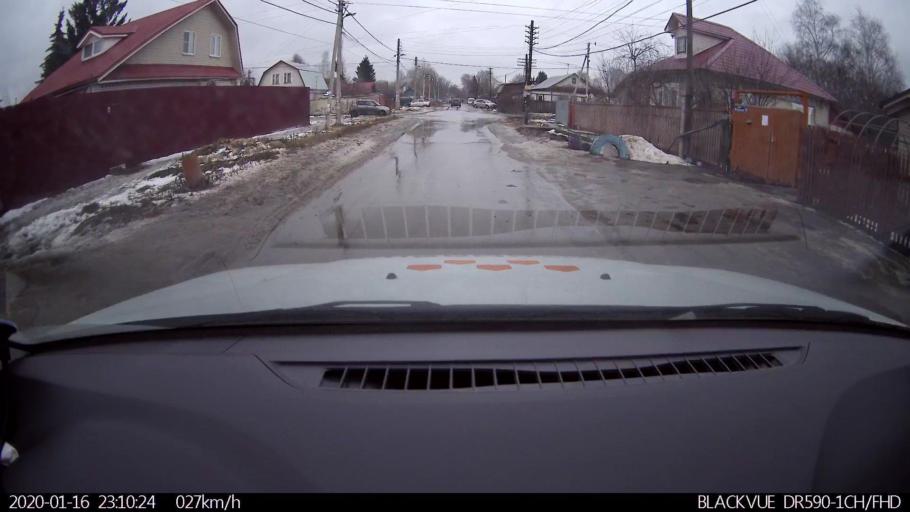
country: RU
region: Nizjnij Novgorod
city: Nizhniy Novgorod
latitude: 56.2866
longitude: 43.9020
